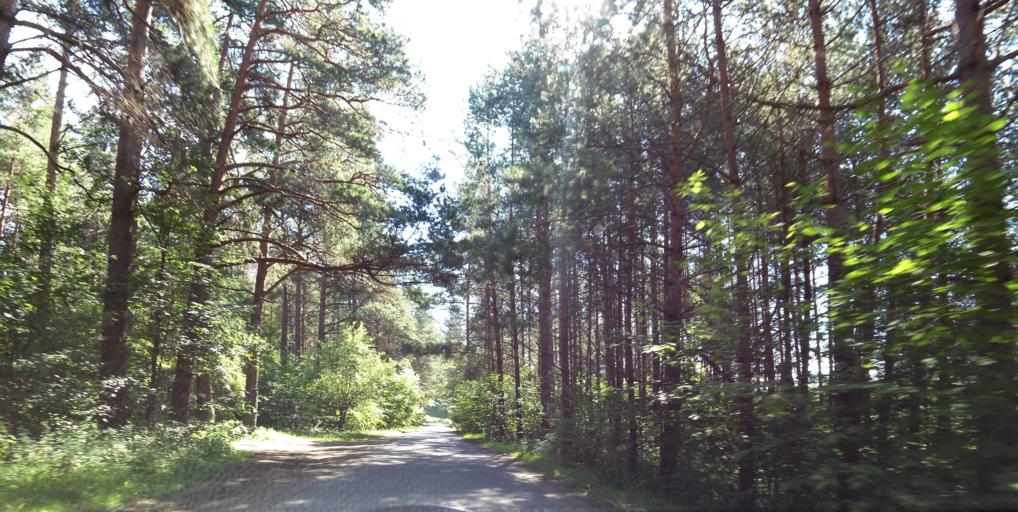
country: LT
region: Vilnius County
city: Rasos
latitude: 54.6904
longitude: 25.3672
